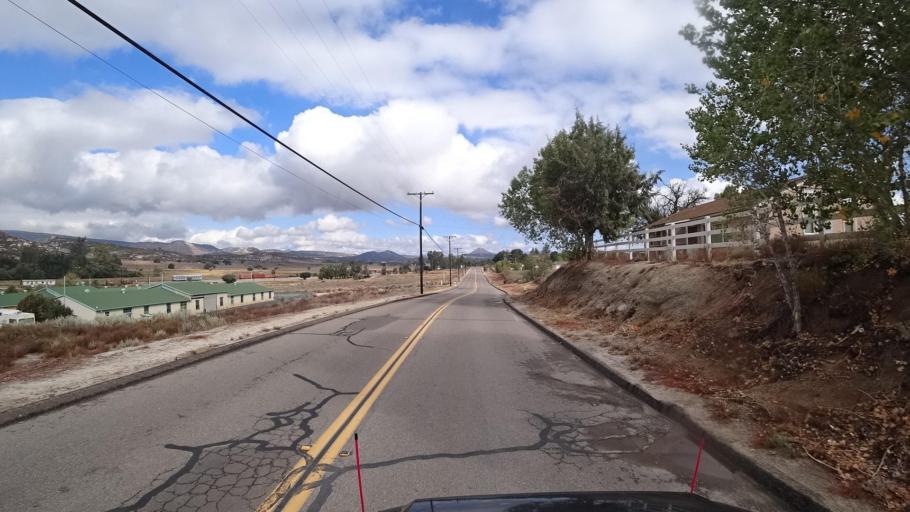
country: US
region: California
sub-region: San Diego County
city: Campo
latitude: 32.6102
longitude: -116.4698
